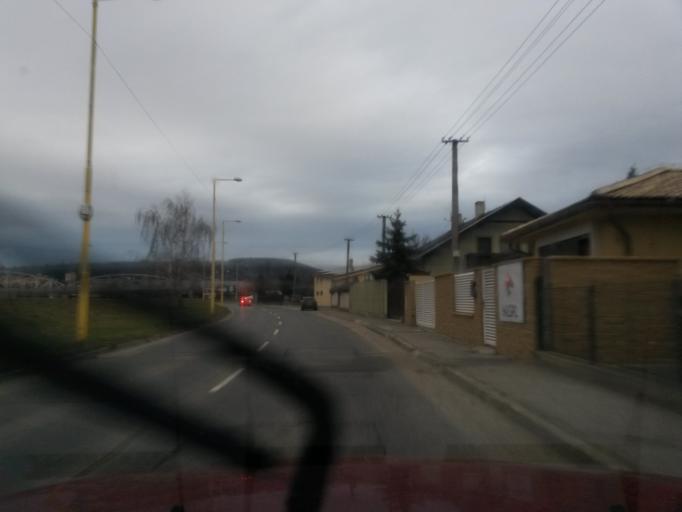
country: SK
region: Kosicky
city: Kosice
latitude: 48.7386
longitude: 21.2653
